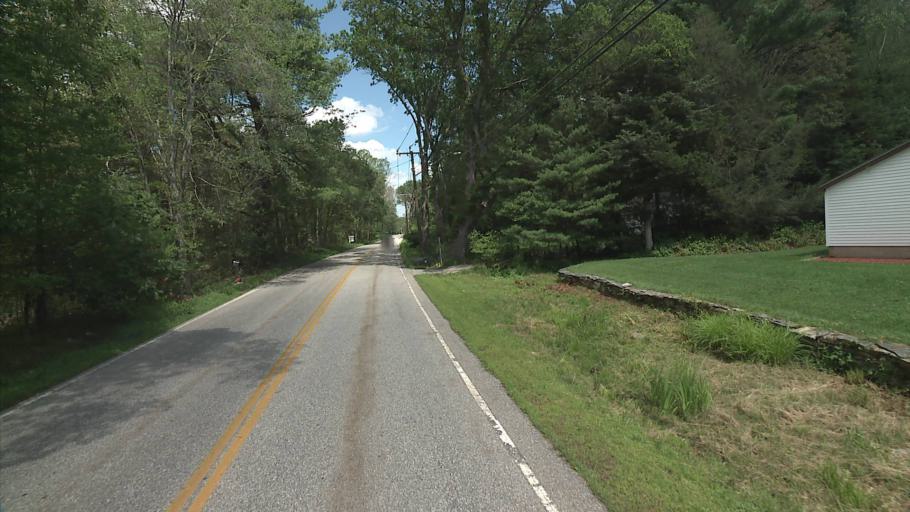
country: US
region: Connecticut
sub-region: Windham County
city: Windham
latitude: 41.7266
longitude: -72.1667
